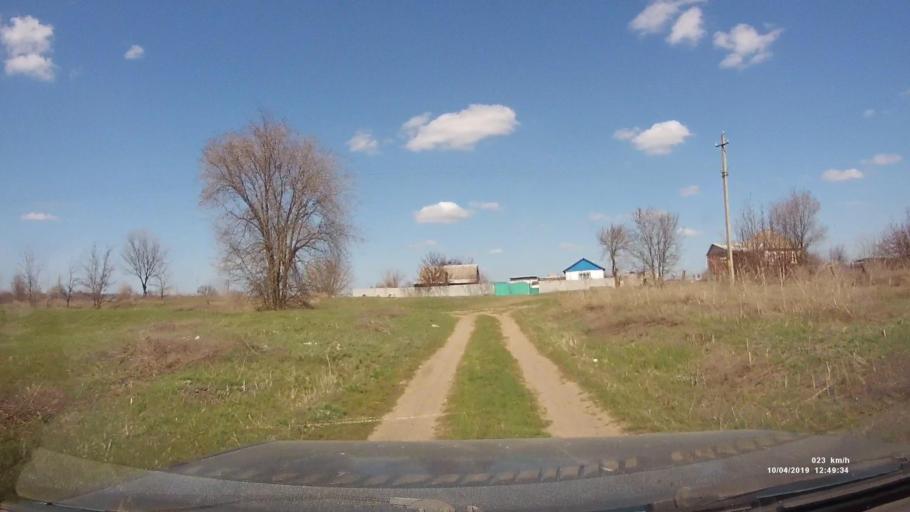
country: RU
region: Rostov
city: Kamensk-Shakhtinskiy
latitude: 48.3580
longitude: 40.2244
